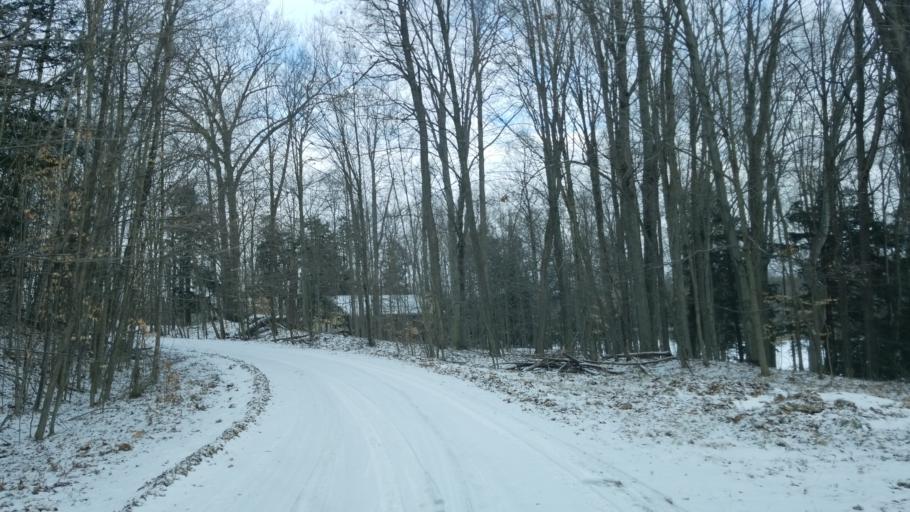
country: US
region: Michigan
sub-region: Osceola County
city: Evart
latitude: 43.8151
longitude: -85.2712
